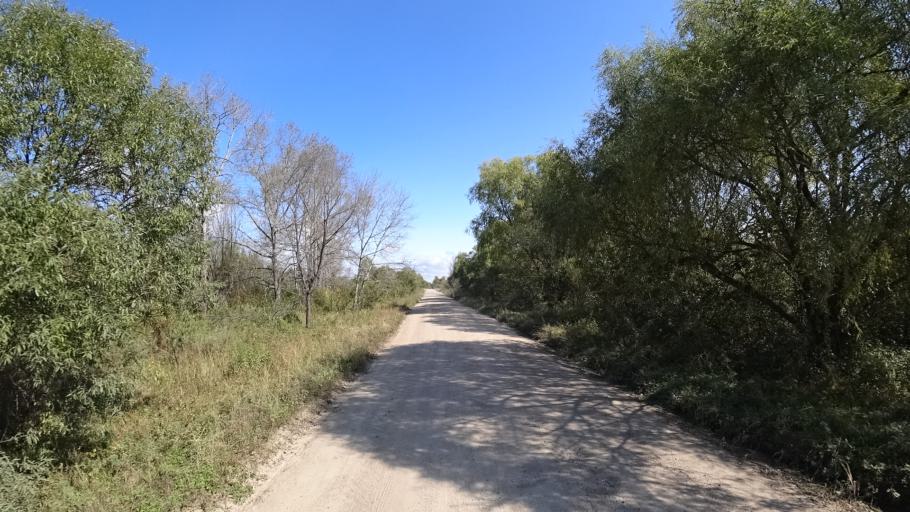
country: RU
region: Amur
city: Arkhara
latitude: 49.4076
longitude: 130.1596
